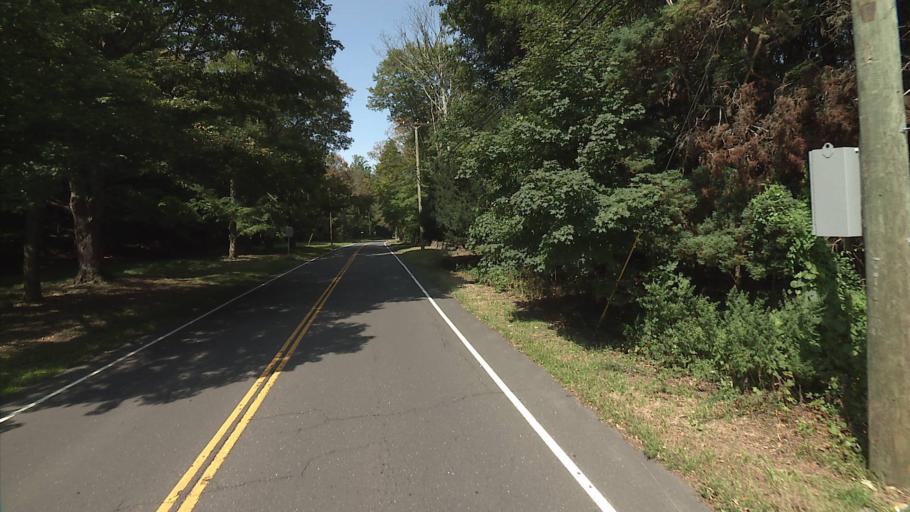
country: US
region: Connecticut
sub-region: Fairfield County
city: Westport
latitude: 41.2478
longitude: -73.3213
